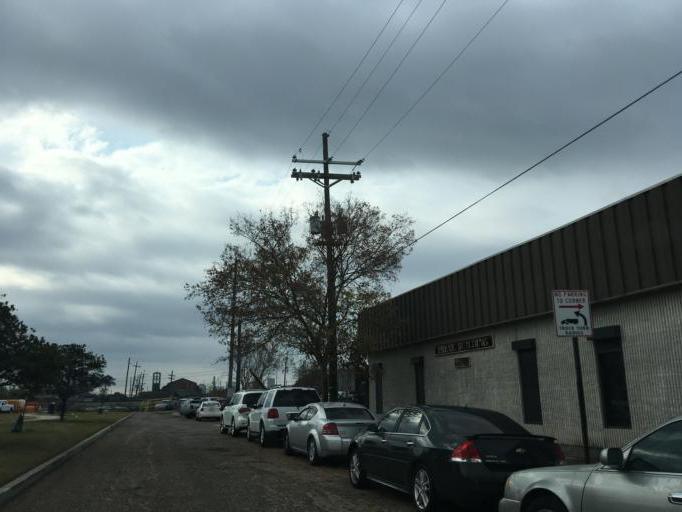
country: US
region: Louisiana
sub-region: Orleans Parish
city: New Orleans
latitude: 29.9885
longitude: -90.0632
